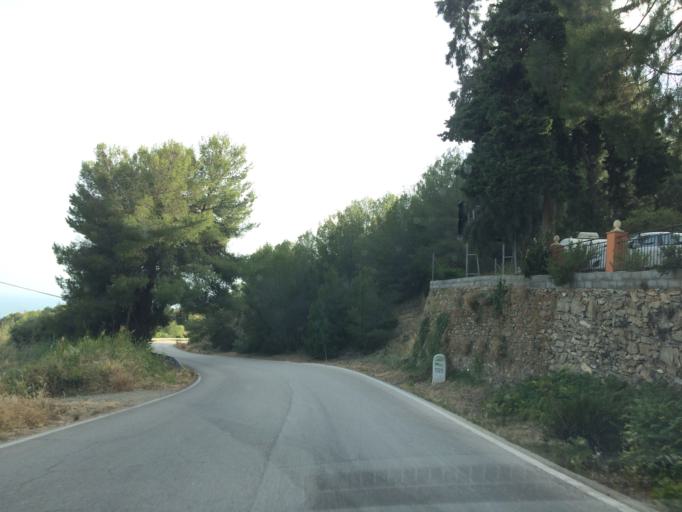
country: ES
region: Andalusia
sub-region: Provincia de Malaga
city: Malaga
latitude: 36.7667
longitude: -4.4049
